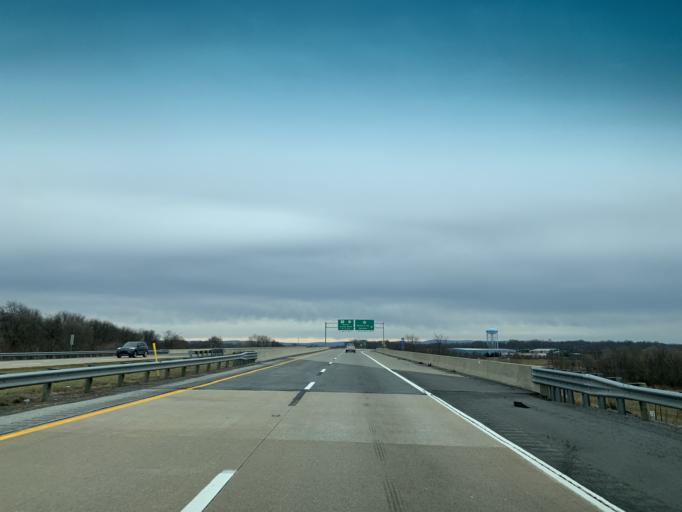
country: US
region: West Virginia
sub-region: Jefferson County
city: Ranson
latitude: 39.3658
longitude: -77.8704
